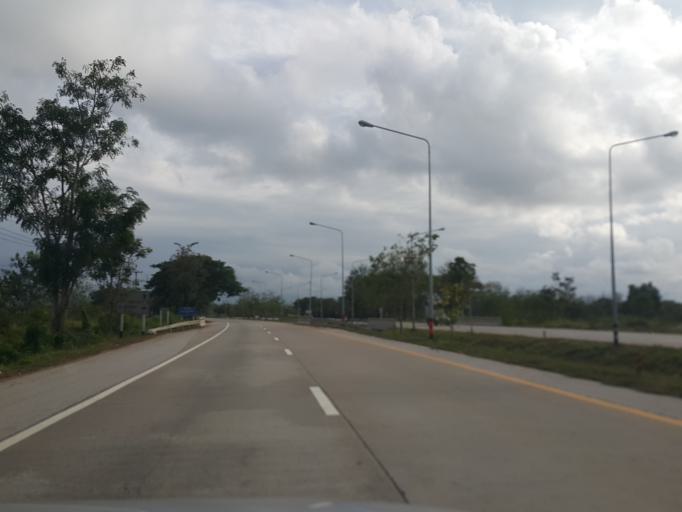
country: TH
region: Lampang
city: Ko Kha
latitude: 18.1932
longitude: 99.4067
